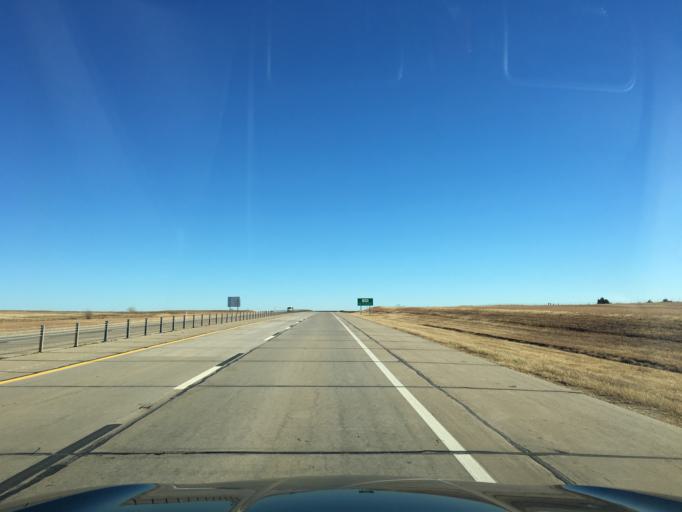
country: US
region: Oklahoma
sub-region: Noble County
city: Perry
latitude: 36.3998
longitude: -97.3088
